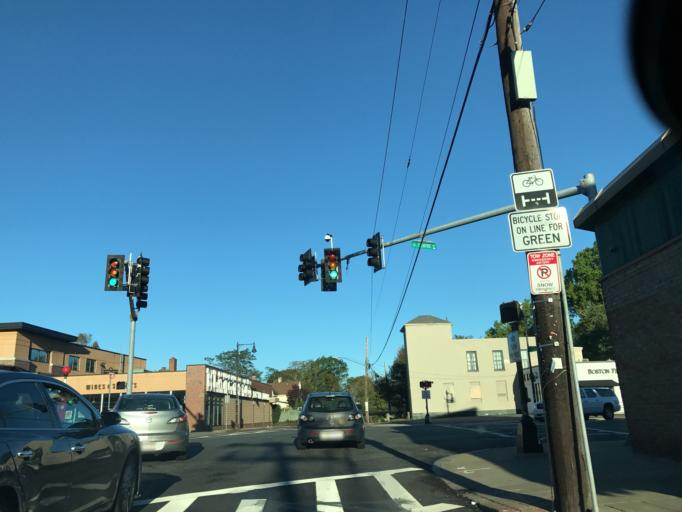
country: US
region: Massachusetts
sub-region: Norfolk County
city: Dedham
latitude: 42.2805
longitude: -71.1579
